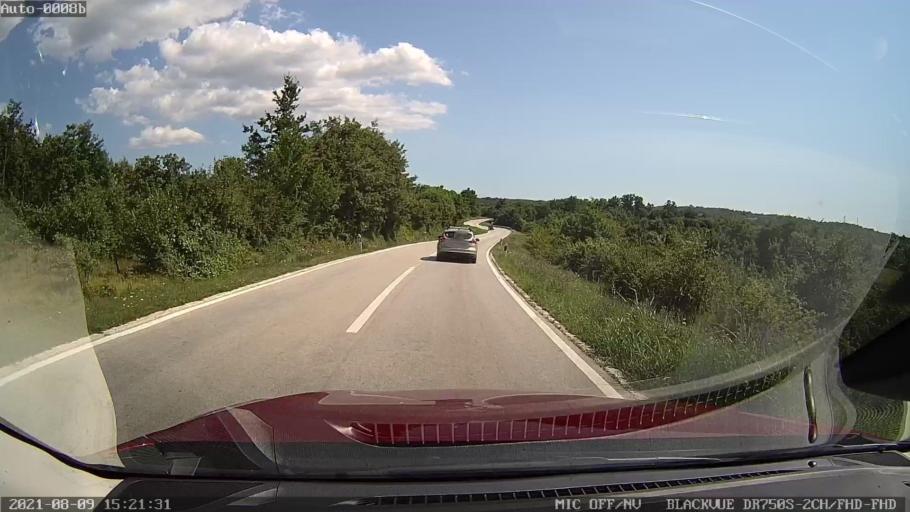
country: HR
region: Istarska
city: Pazin
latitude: 45.1985
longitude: 13.8974
